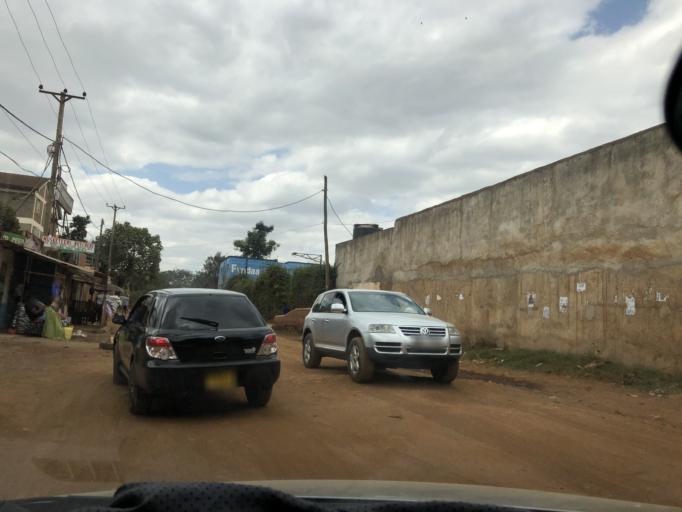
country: KE
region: Nairobi Area
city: Pumwani
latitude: -1.2315
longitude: 36.8756
